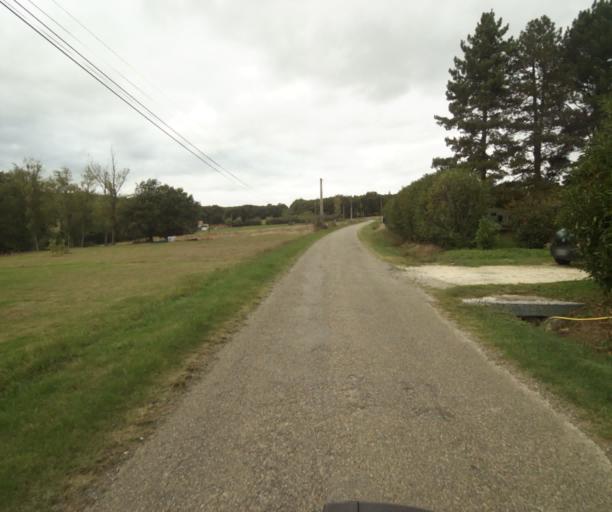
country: FR
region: Midi-Pyrenees
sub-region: Departement du Tarn-et-Garonne
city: Beaumont-de-Lomagne
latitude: 43.8418
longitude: 1.1041
